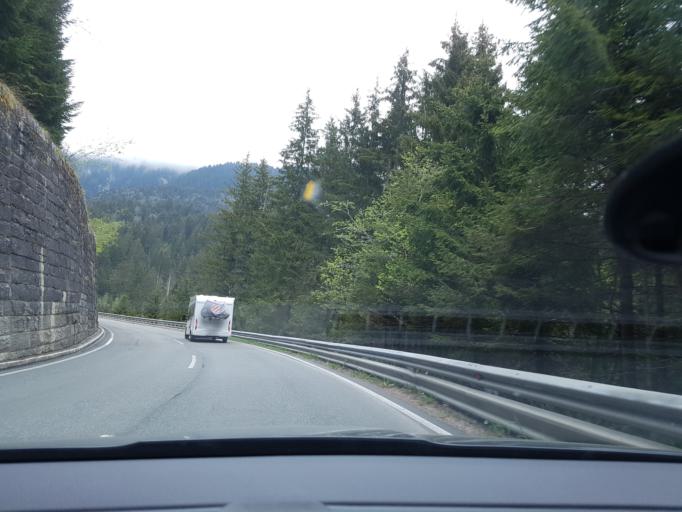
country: AT
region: Salzburg
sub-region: Politischer Bezirk Zell am See
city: Krimml
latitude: 47.2185
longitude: 12.1614
